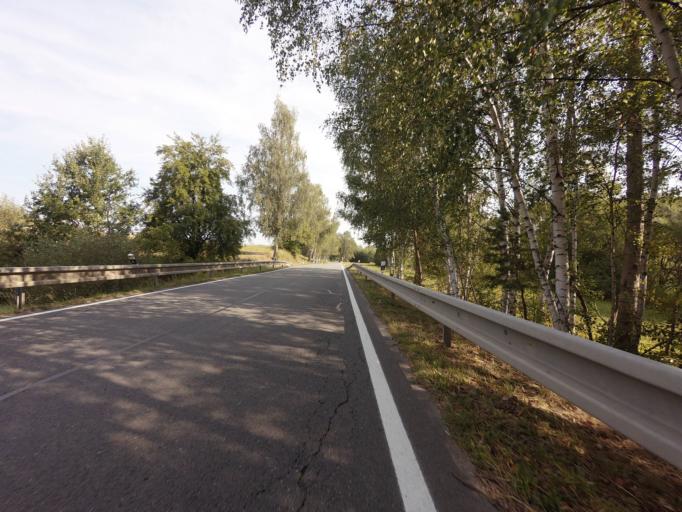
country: CZ
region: Jihocesky
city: Milevsko
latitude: 49.4699
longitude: 14.3616
